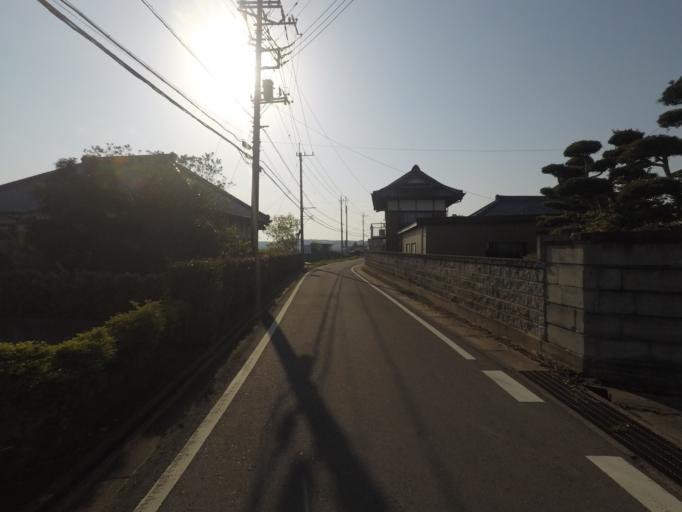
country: JP
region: Ibaraki
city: Inashiki
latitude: 36.0682
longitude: 140.3186
